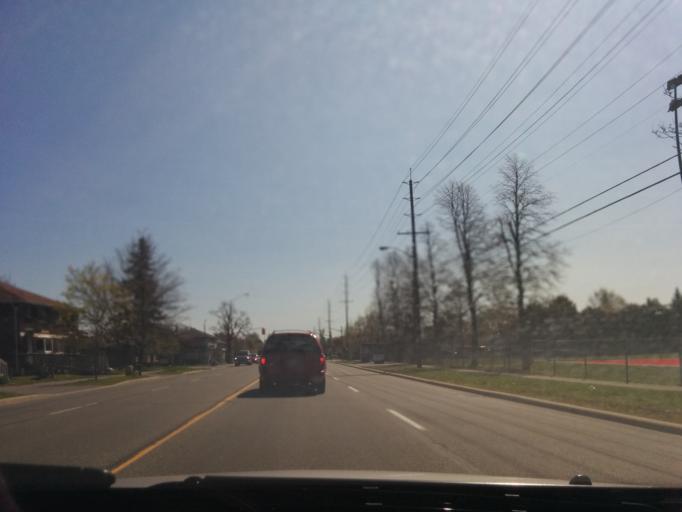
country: CA
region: Ontario
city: Ottawa
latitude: 45.3999
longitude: -75.6403
